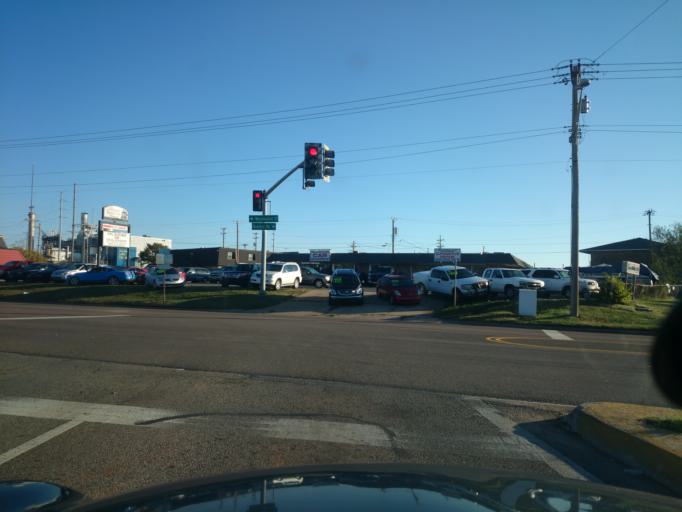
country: US
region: Oklahoma
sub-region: Payne County
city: Stillwater
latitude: 36.1421
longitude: -97.0688
